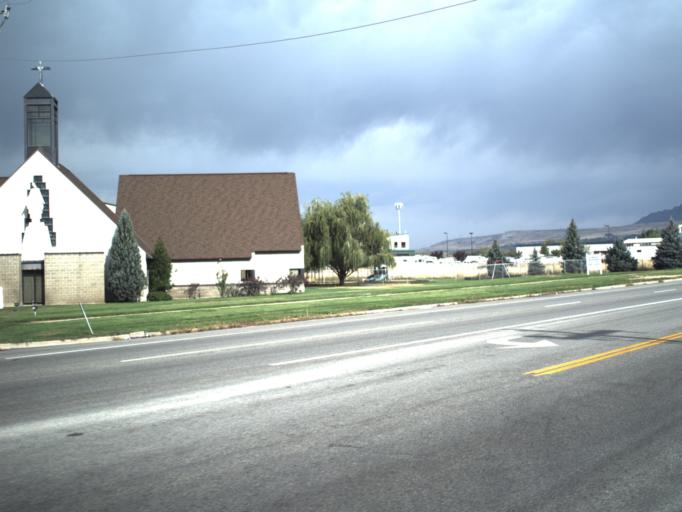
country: US
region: Utah
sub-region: Weber County
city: Harrisville
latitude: 41.2772
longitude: -111.9692
